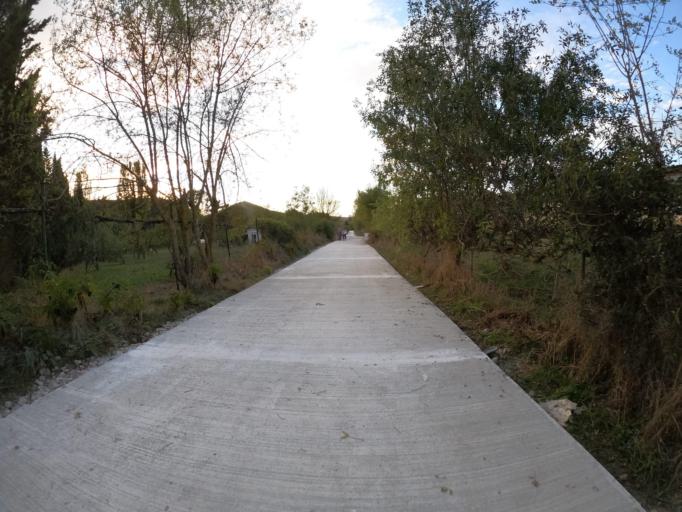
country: ES
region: Navarre
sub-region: Provincia de Navarra
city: Egues-Uharte
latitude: 42.8334
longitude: -1.5768
